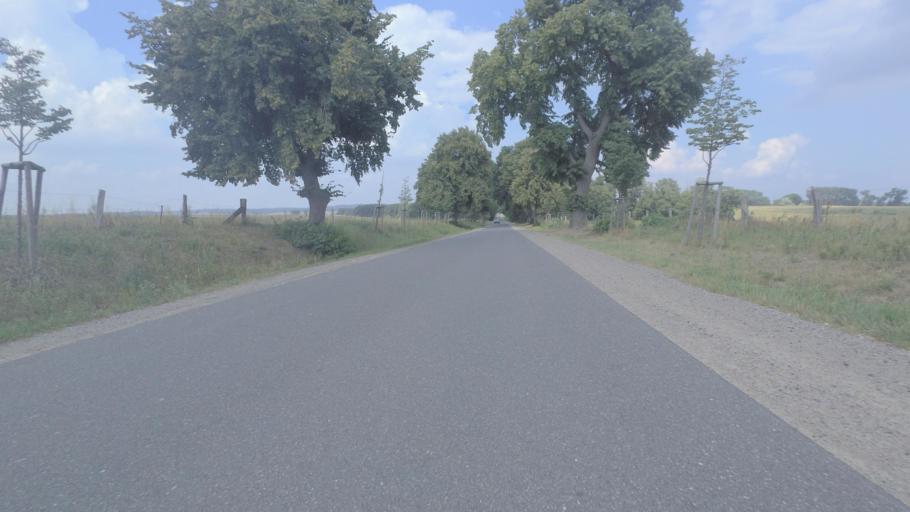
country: DE
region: Mecklenburg-Vorpommern
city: Malchin
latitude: 53.7594
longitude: 12.8368
